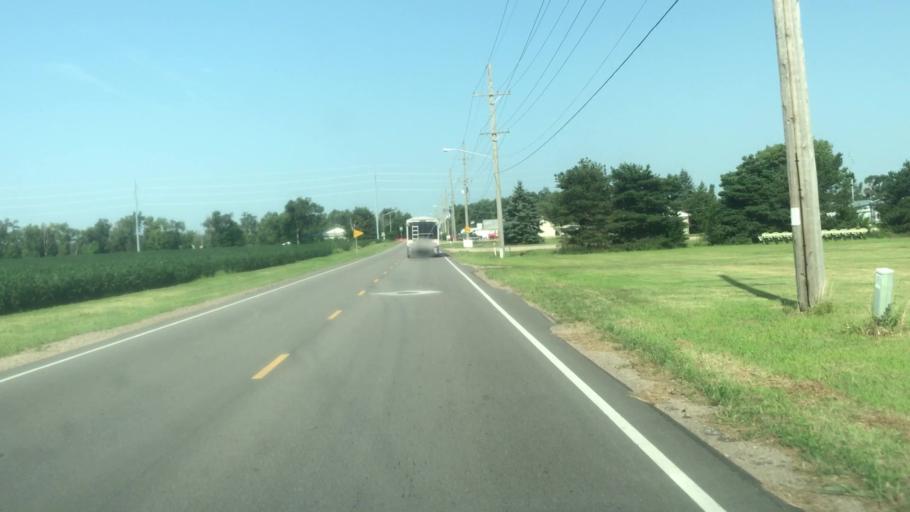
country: US
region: Nebraska
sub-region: Hall County
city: Grand Island
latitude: 40.9456
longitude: -98.3300
